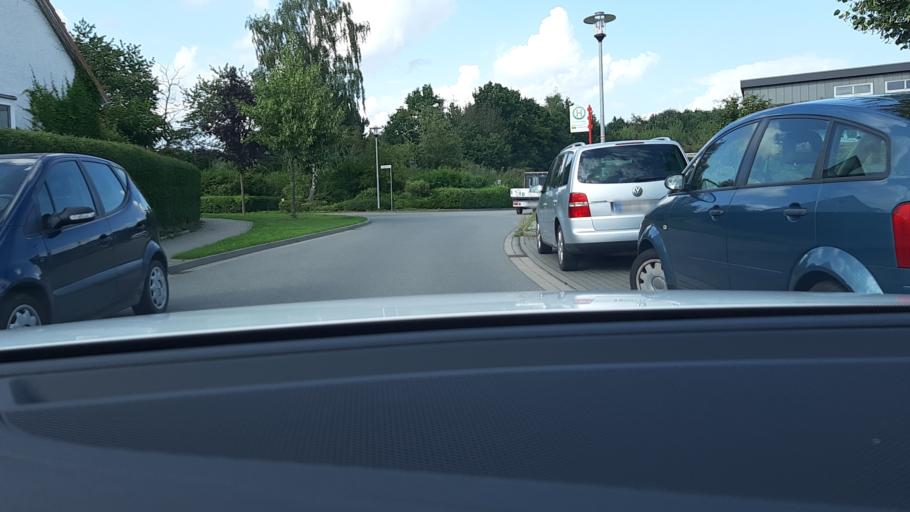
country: DE
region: Schleswig-Holstein
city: Heidekamp
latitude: 53.8373
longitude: 10.5050
